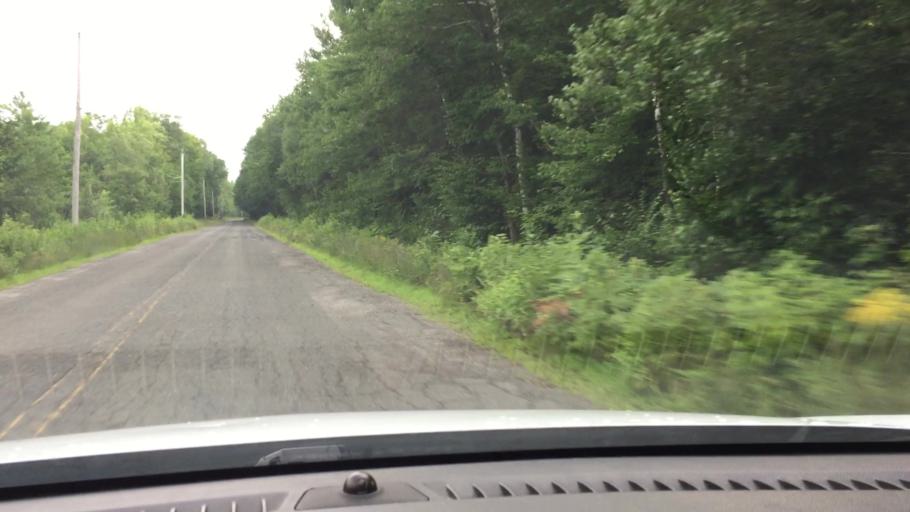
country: US
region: Massachusetts
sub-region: Hampshire County
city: Chesterfield
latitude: 42.2784
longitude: -72.9133
